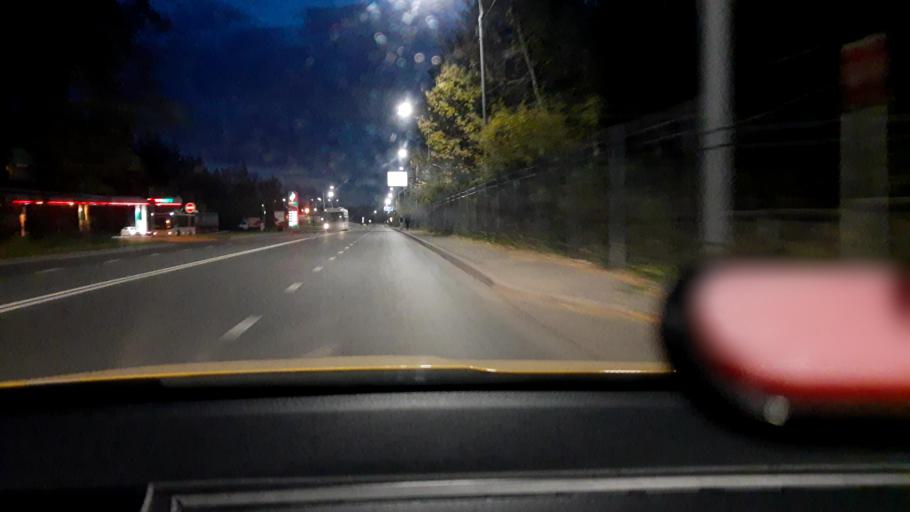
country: RU
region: Moskovskaya
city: Krasnoznamensk
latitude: 55.6047
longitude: 37.0498
